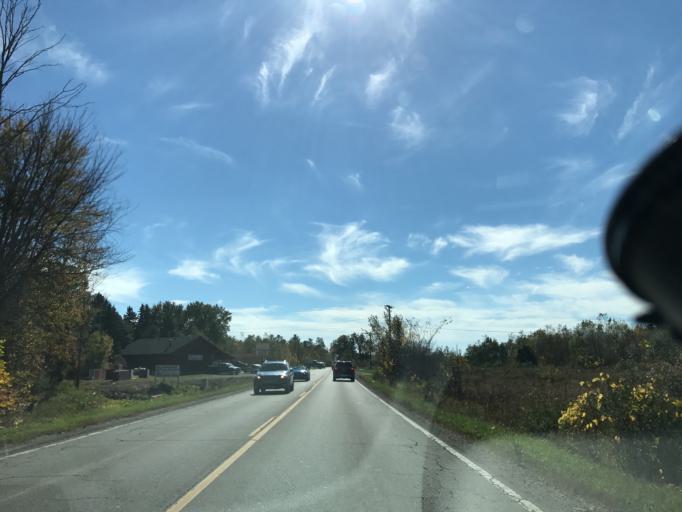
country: US
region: Michigan
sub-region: Oakland County
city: South Lyon
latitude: 42.4153
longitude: -83.6465
